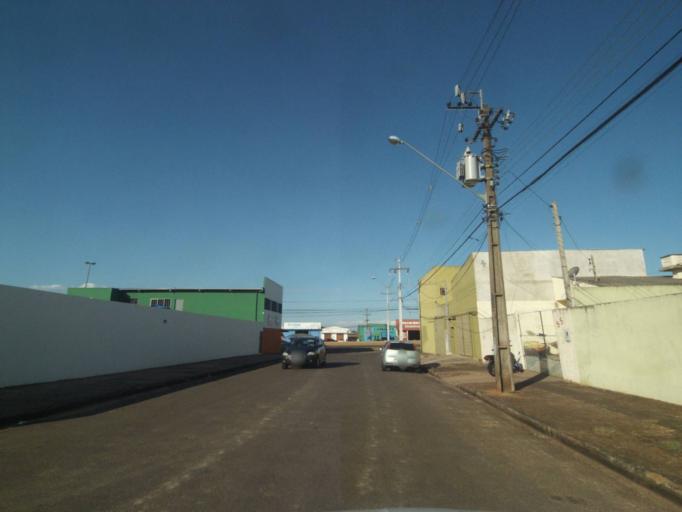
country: BR
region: Parana
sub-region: Londrina
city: Londrina
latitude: -23.3091
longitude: -51.2206
